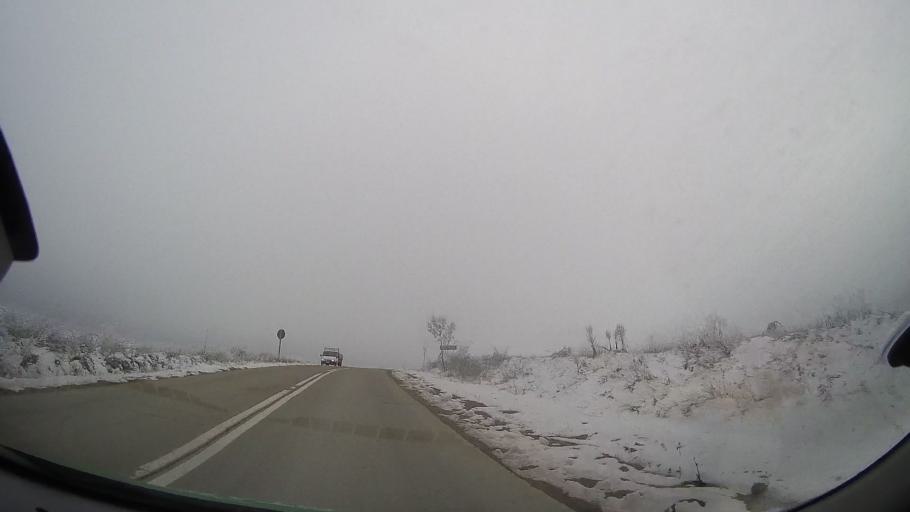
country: RO
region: Vaslui
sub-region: Comuna Ivesti
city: Ivesti
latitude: 46.2051
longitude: 27.5070
